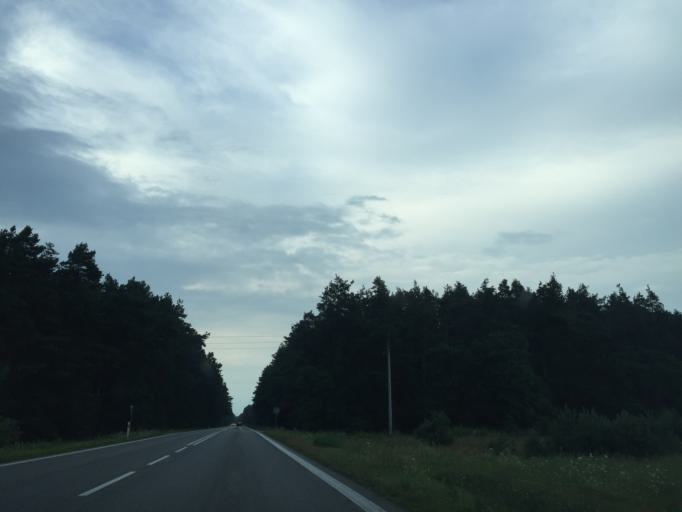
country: PL
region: Masovian Voivodeship
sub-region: Powiat ostrowski
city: Brok
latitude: 52.7534
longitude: 21.8567
